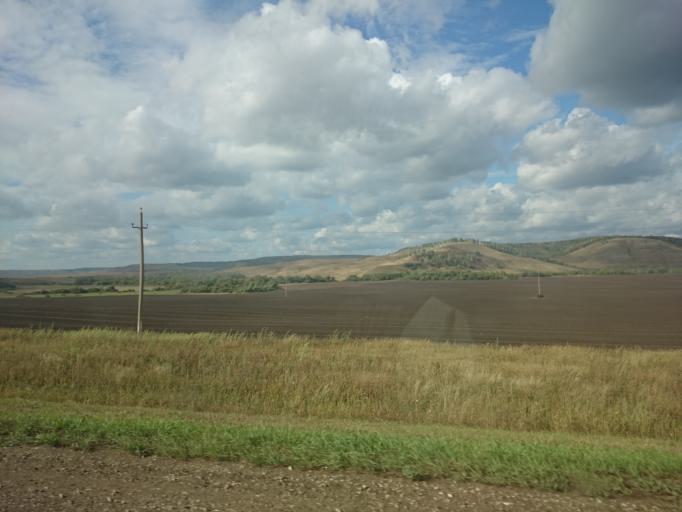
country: RU
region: Samara
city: Kamyshla
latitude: 54.0723
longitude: 52.2092
